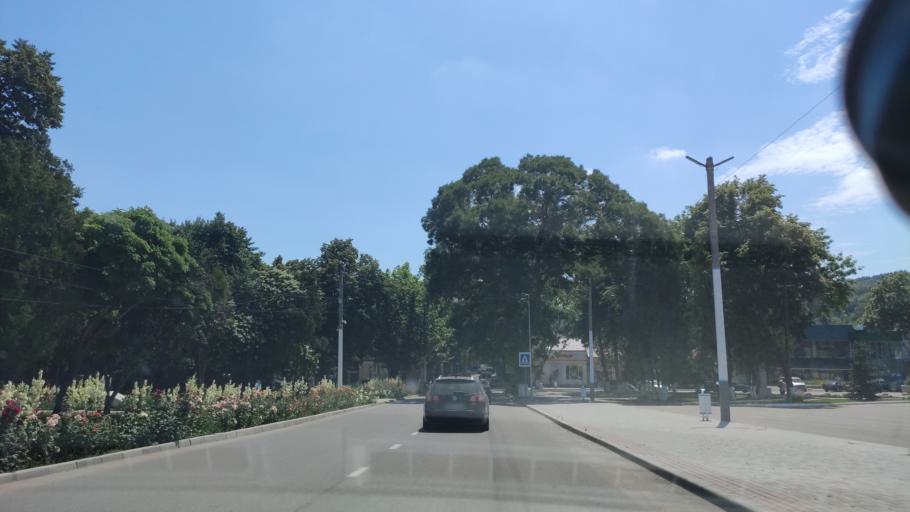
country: MD
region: Raionul Soroca
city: Soroca
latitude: 48.1572
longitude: 28.3000
